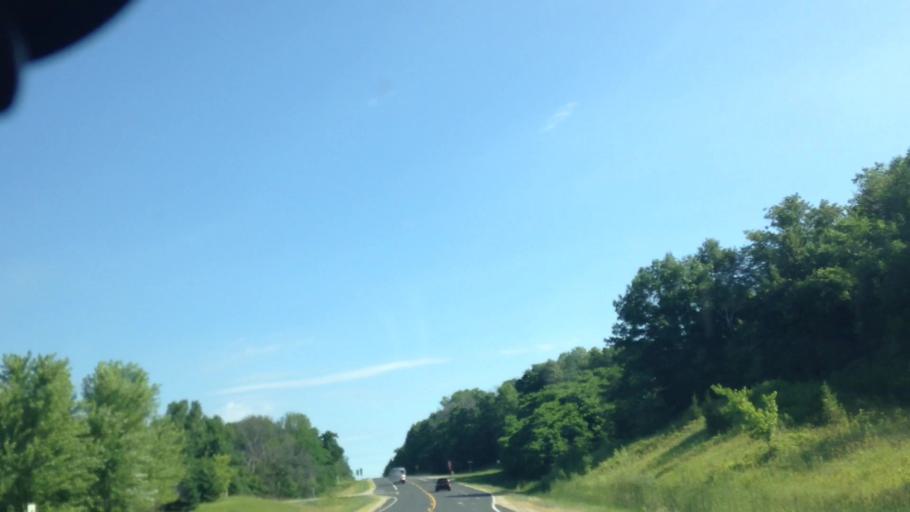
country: US
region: Wisconsin
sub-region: Washington County
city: Slinger
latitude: 43.3677
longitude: -88.2589
